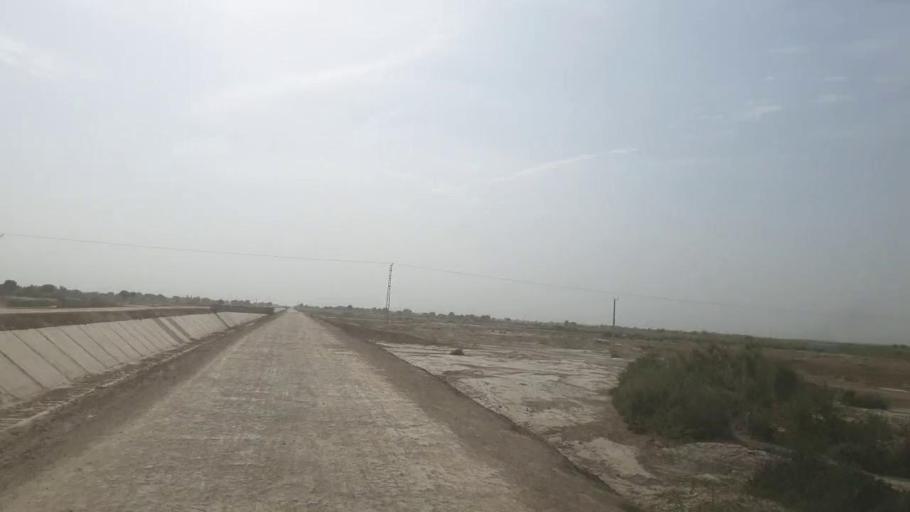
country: PK
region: Sindh
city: Nabisar
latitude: 25.0496
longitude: 69.5243
